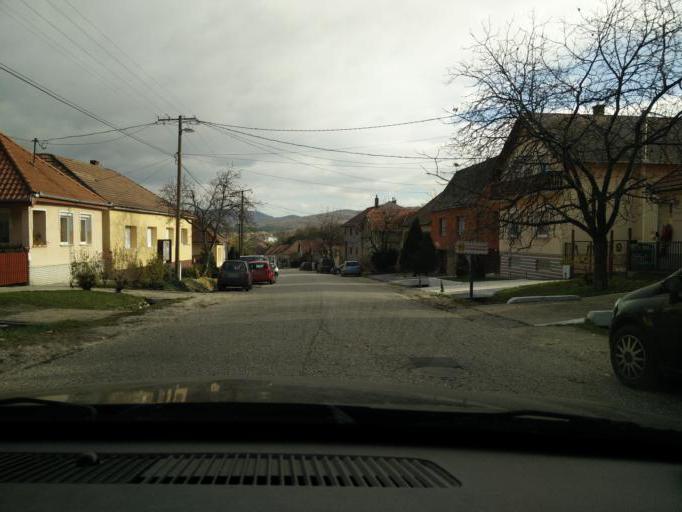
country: HU
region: Komarom-Esztergom
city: Kesztolc
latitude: 47.6794
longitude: 18.7720
